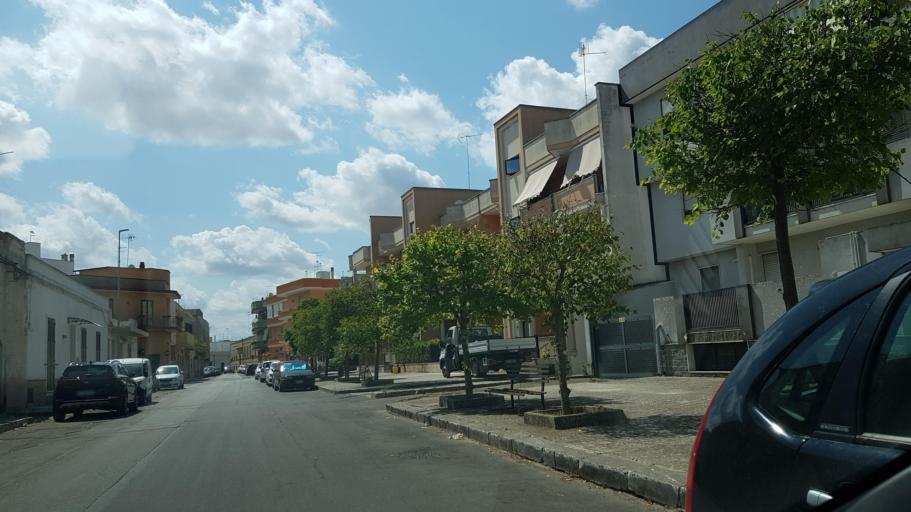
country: IT
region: Apulia
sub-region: Provincia di Lecce
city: Trepuzzi
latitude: 40.4095
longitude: 18.0749
